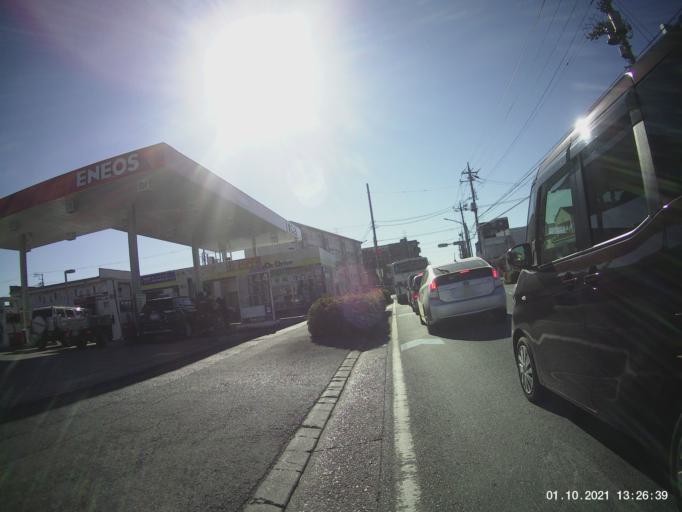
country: JP
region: Chiba
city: Yotsukaido
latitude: 35.6020
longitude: 140.2090
